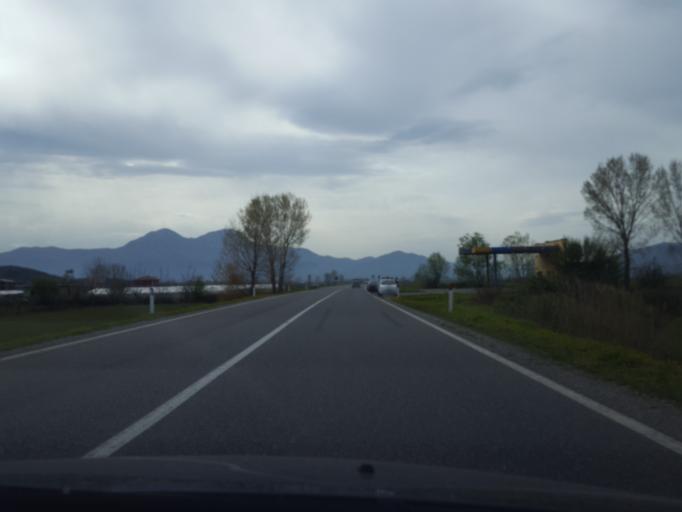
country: AL
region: Lezhe
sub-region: Rrethi i Lezhes
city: Dajc
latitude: 41.9106
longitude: 19.5992
